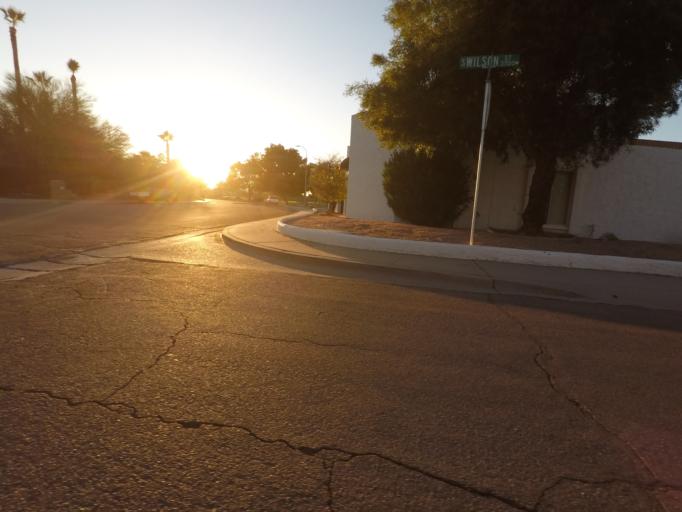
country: US
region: Arizona
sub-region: Maricopa County
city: Guadalupe
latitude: 33.3893
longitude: -111.9463
